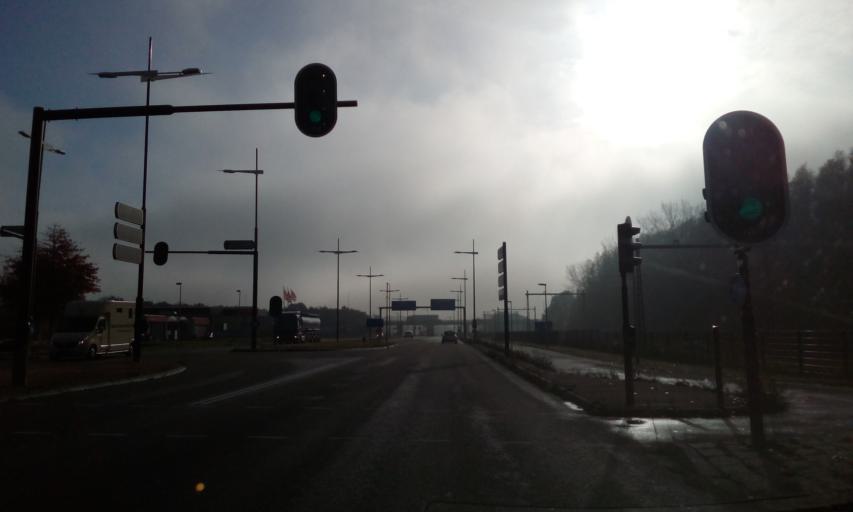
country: NL
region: Gelderland
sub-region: Gemeente Lochem
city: Epse
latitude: 52.2395
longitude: 6.2097
